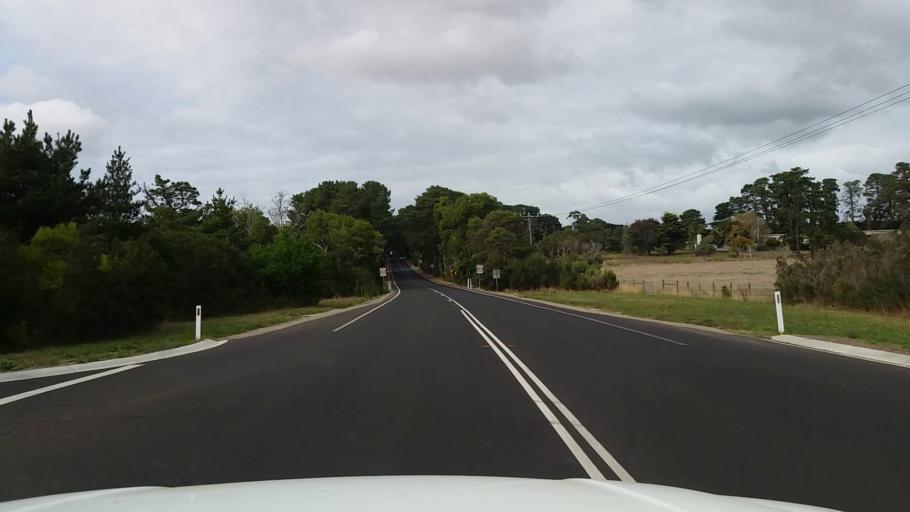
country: AU
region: Victoria
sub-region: Mornington Peninsula
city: Balnarring
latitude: -38.3537
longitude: 145.1076
